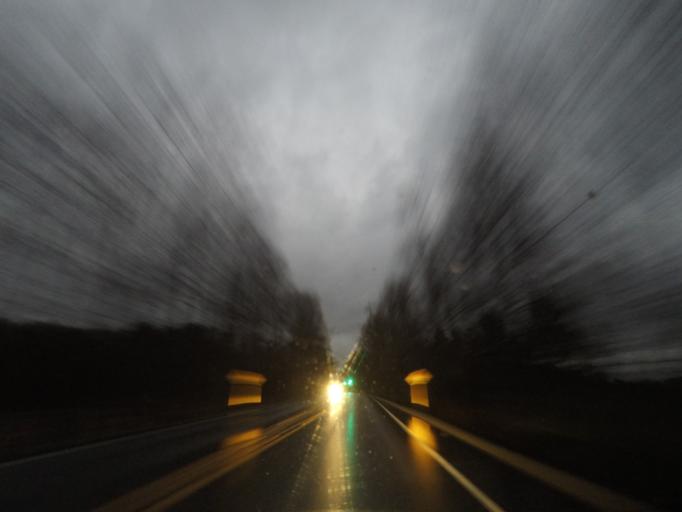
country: US
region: North Carolina
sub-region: Orange County
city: Hillsborough
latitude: 36.0680
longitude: -79.0617
